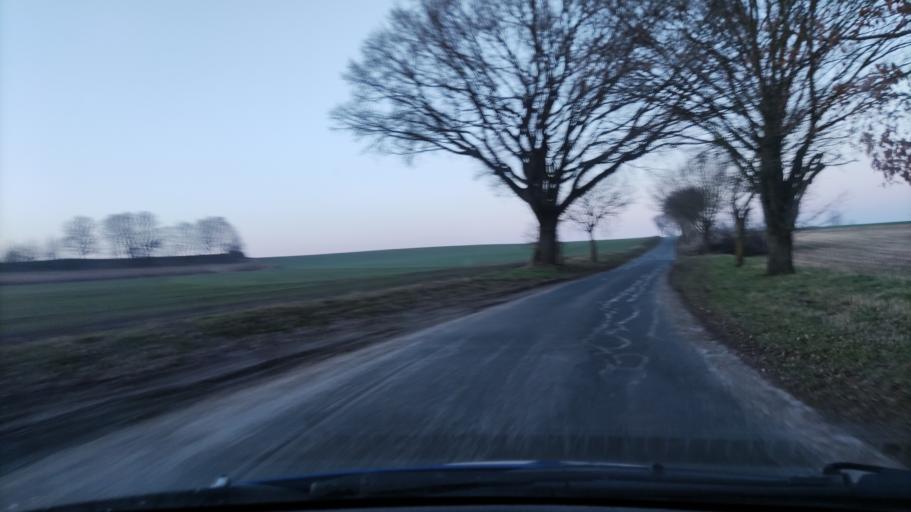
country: DE
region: Lower Saxony
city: Natendorf
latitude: 53.0482
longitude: 10.4782
